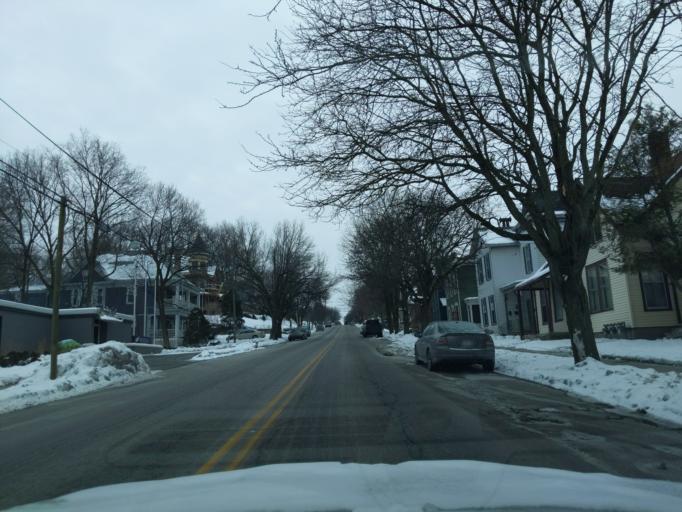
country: US
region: Indiana
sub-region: Tippecanoe County
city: Lafayette
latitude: 40.4167
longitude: -86.8867
